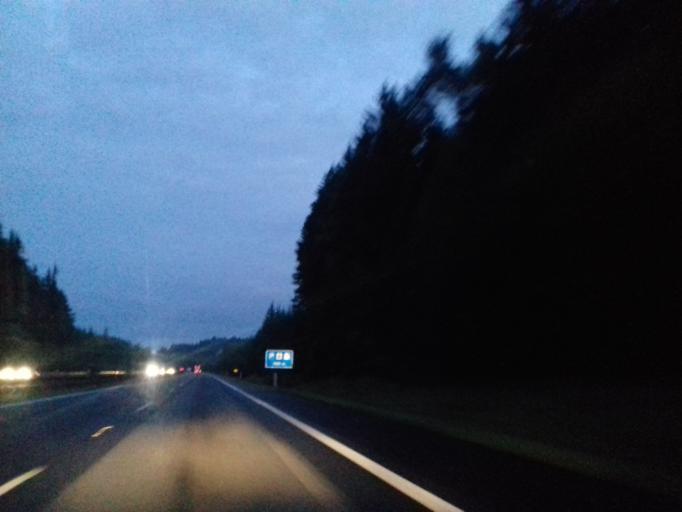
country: CZ
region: Vysocina
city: Vilemov
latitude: 49.5195
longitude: 15.3914
